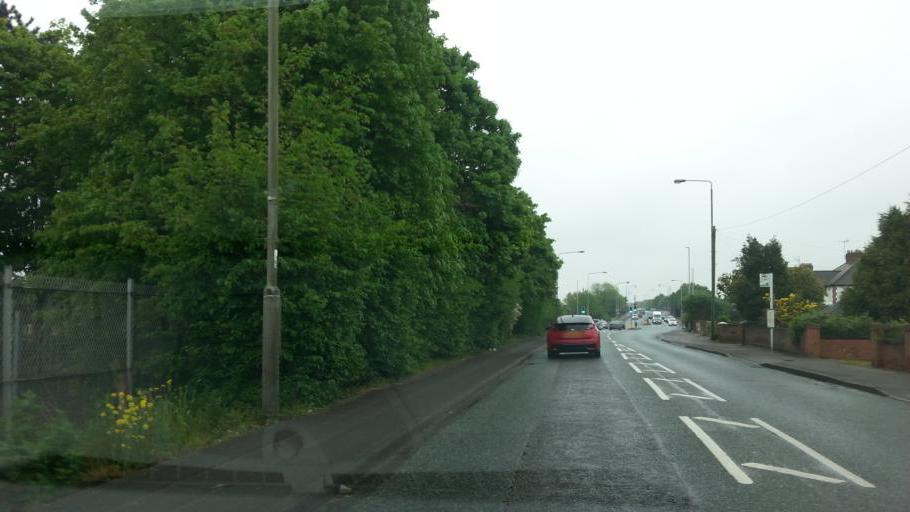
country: GB
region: England
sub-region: Nottinghamshire
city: Newark on Trent
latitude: 53.0865
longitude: -0.7974
